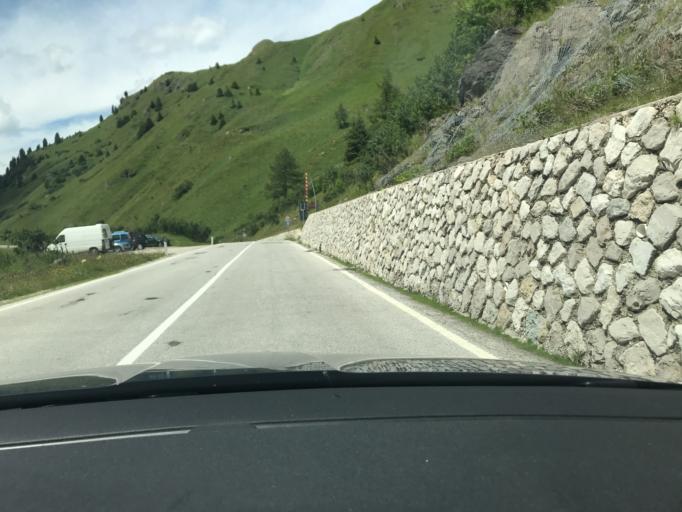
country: IT
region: Veneto
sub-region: Provincia di Belluno
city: Livinallongo del Col di Lana
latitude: 46.4545
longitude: 11.8865
